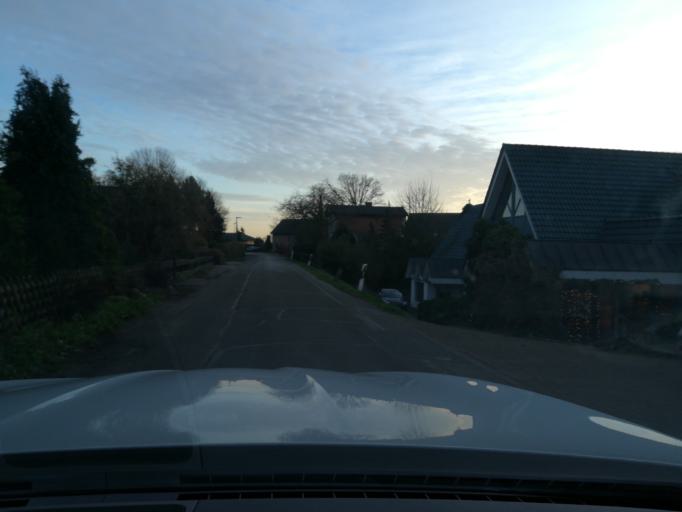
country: DE
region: Lower Saxony
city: Stelle
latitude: 53.4420
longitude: 10.0817
